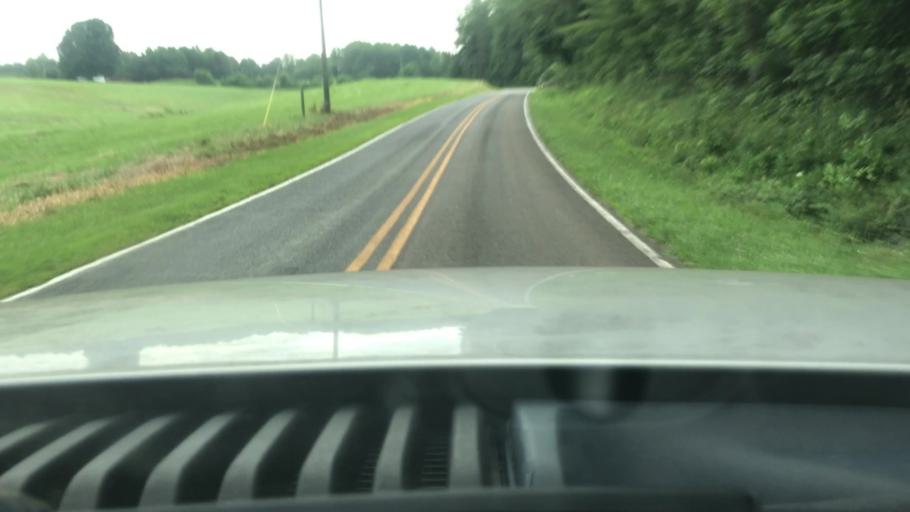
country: US
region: North Carolina
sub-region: Surry County
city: Thurmond
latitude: 36.4174
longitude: -80.8332
